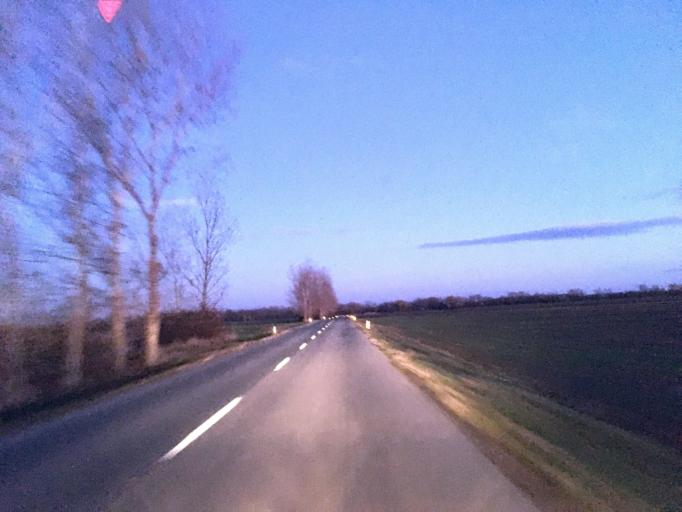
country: SK
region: Nitriansky
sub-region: Okres Komarno
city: Hurbanovo
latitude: 47.8968
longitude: 18.1726
